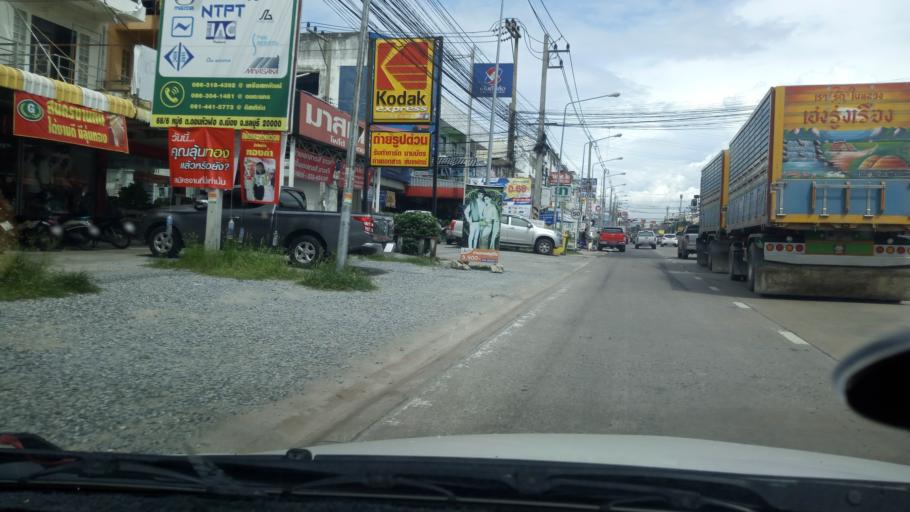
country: TH
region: Chon Buri
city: Phan Thong
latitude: 13.4313
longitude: 101.0367
